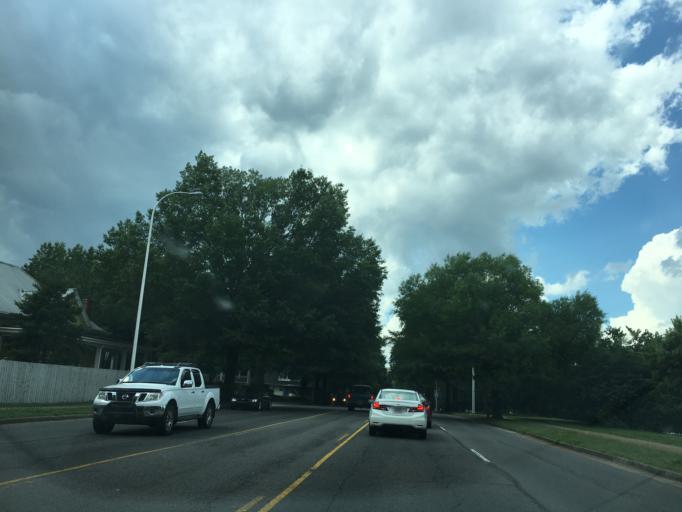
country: US
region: Tennessee
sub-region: Davidson County
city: Nashville
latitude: 36.1400
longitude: -86.8135
